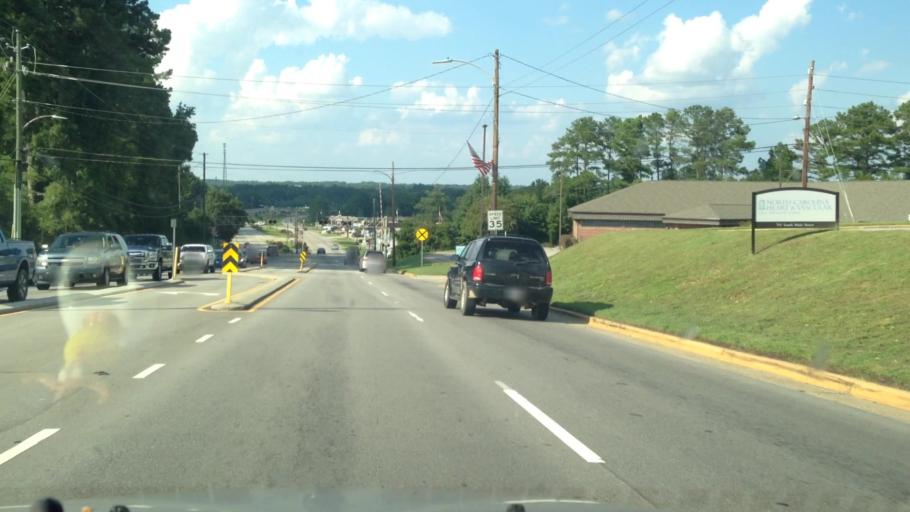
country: US
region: North Carolina
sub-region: Harnett County
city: Lillington
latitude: 35.3994
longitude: -78.8159
